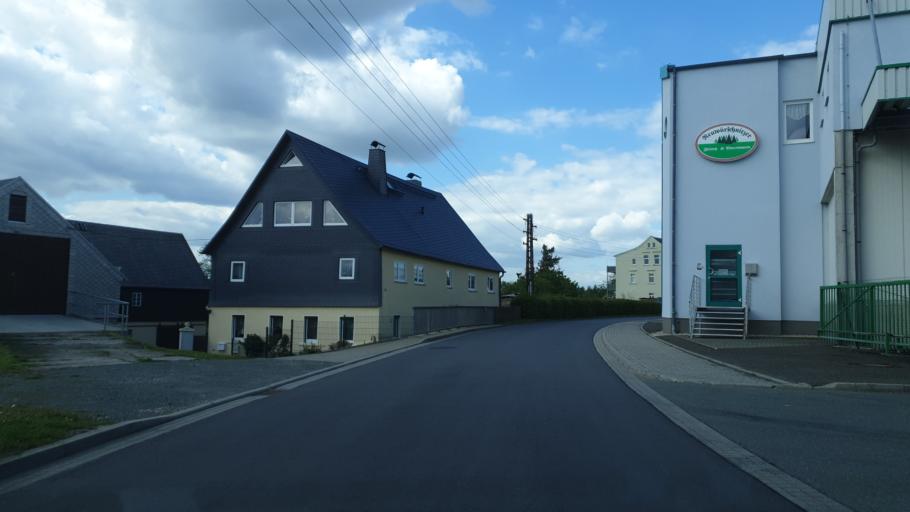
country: DE
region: Saxony
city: Lugau
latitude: 50.7122
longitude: 12.7429
